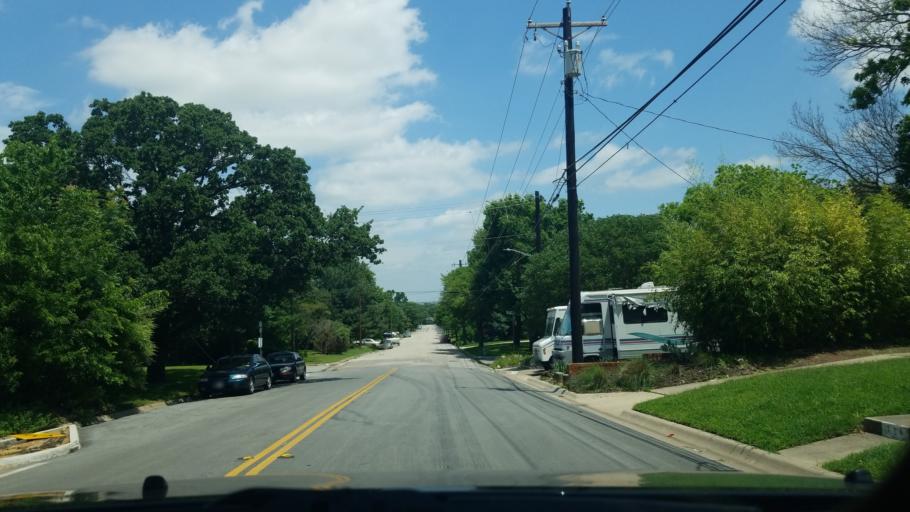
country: US
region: Texas
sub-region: Denton County
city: Denton
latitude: 33.2212
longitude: -97.1587
